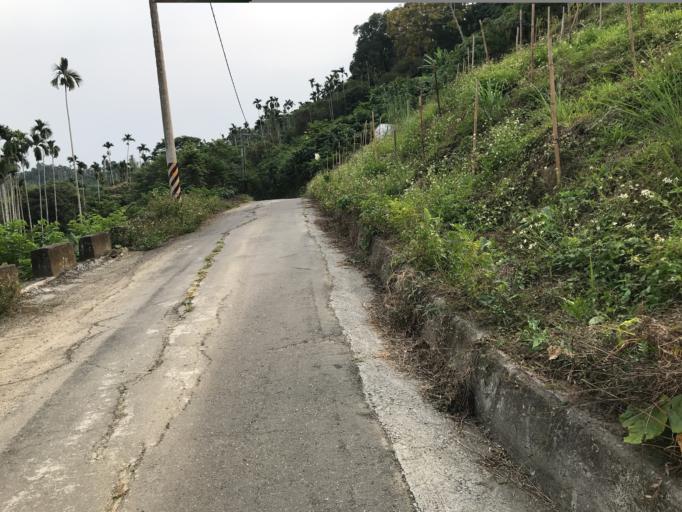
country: TW
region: Taiwan
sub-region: Chiayi
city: Jiayi Shi
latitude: 23.4269
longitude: 120.5260
